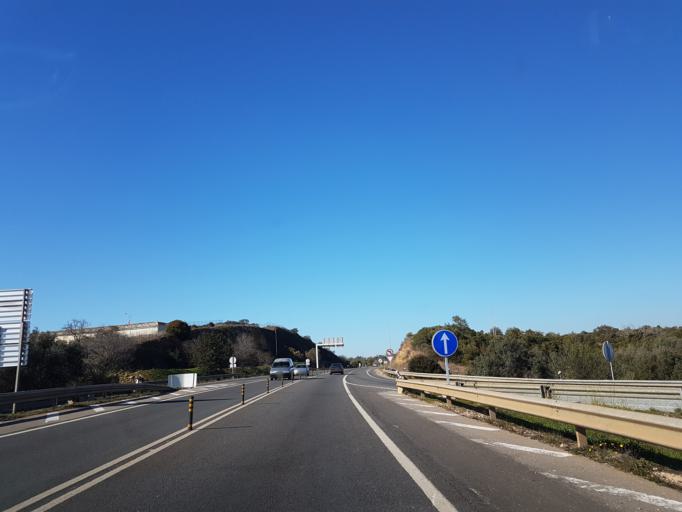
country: PT
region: Faro
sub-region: Portimao
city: Portimao
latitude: 37.1567
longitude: -8.5389
